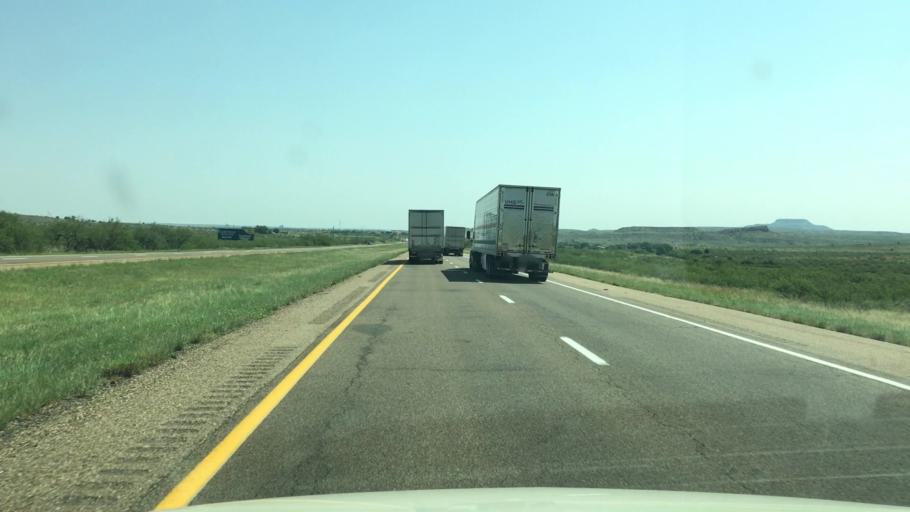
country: US
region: New Mexico
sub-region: Quay County
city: Tucumcari
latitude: 35.1411
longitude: -103.8221
